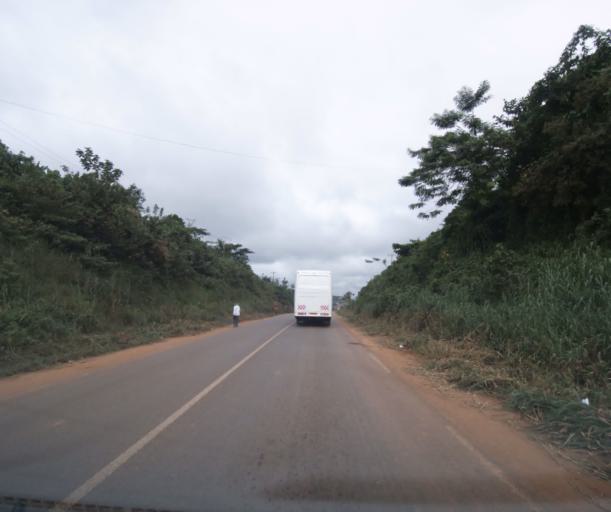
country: CM
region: Centre
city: Yaounde
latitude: 3.7956
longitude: 11.4963
